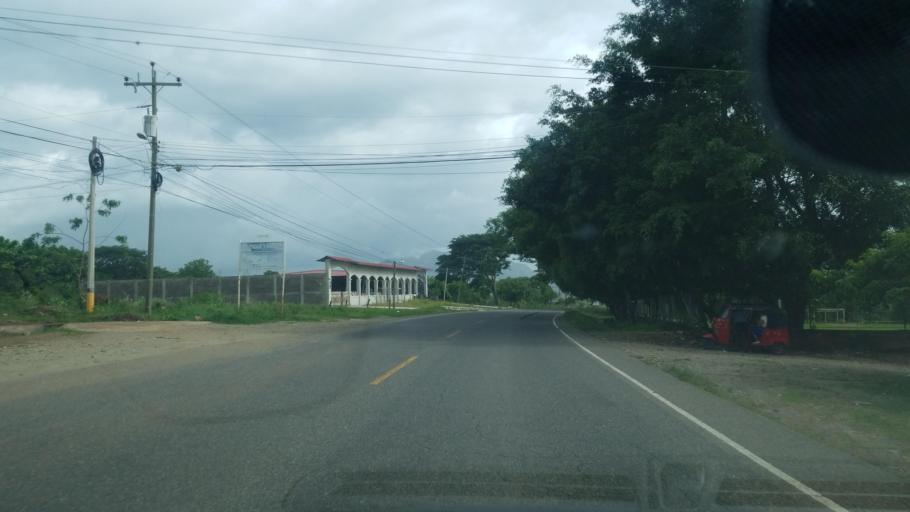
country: HN
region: Ocotepeque
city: Antigua Ocotepeque
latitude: 14.4018
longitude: -89.1963
